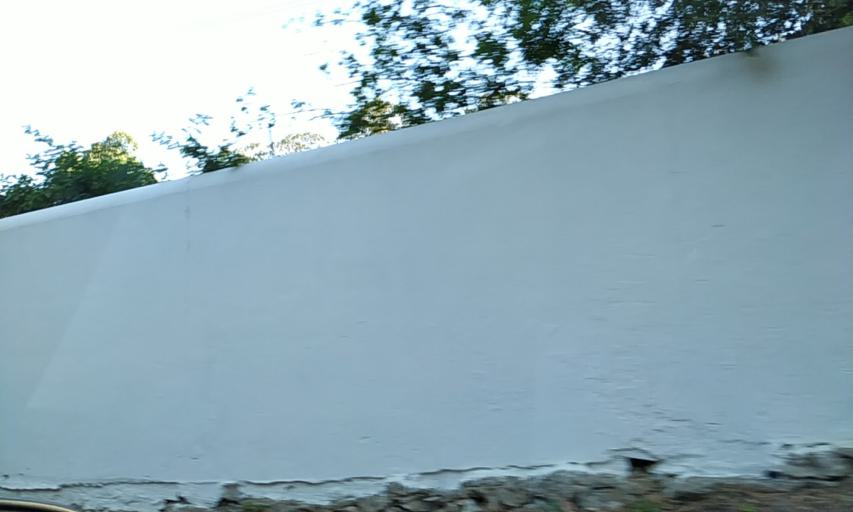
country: PT
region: Santarem
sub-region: Santarem
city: Santarem
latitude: 39.2565
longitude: -8.6762
